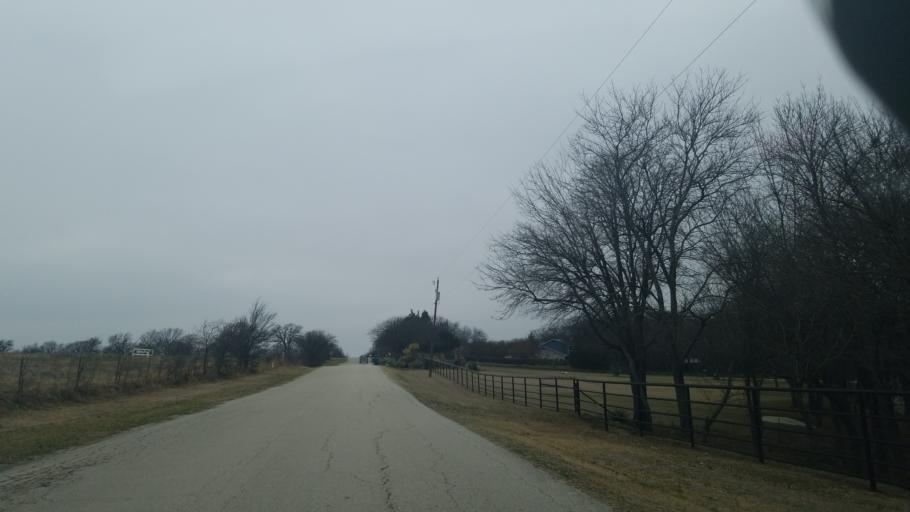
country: US
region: Texas
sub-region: Denton County
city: Argyle
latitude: 33.1472
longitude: -97.1487
